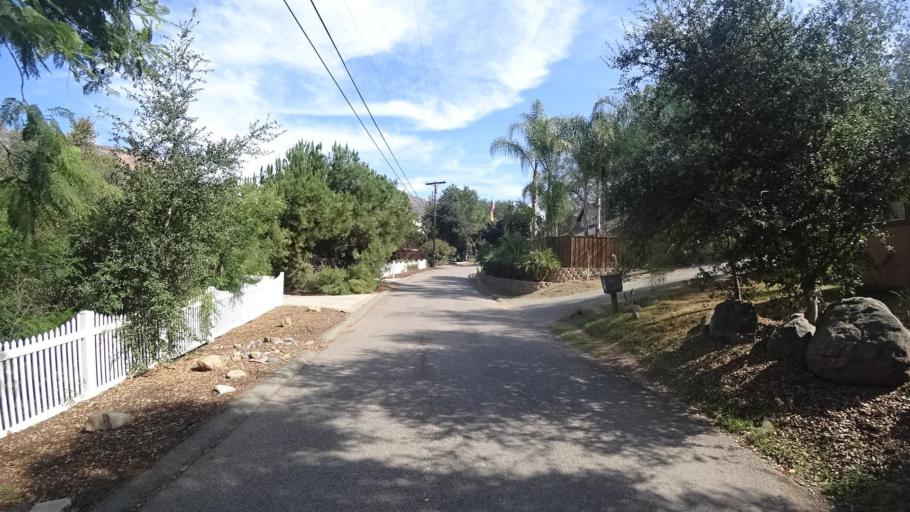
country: US
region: California
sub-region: San Diego County
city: Harbison Canyon
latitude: 32.8185
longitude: -116.8301
